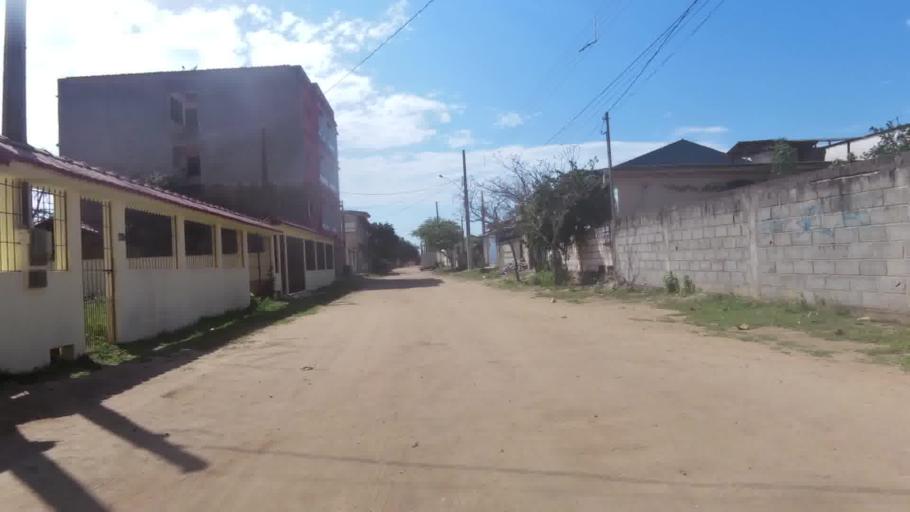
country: BR
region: Espirito Santo
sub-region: Piuma
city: Piuma
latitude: -20.8431
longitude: -40.7396
